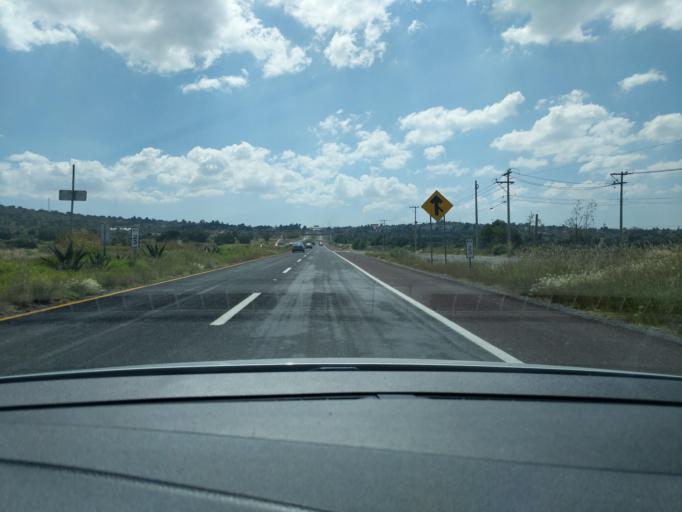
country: MX
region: Hidalgo
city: Zempoala
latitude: 19.9307
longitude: -98.6837
